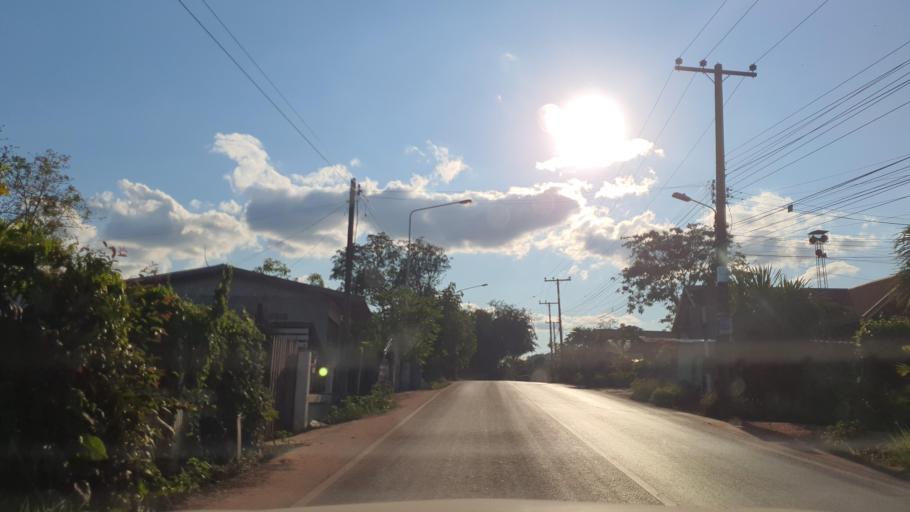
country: TH
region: Changwat Bueng Kan
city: Si Wilai
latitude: 18.1512
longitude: 103.9031
